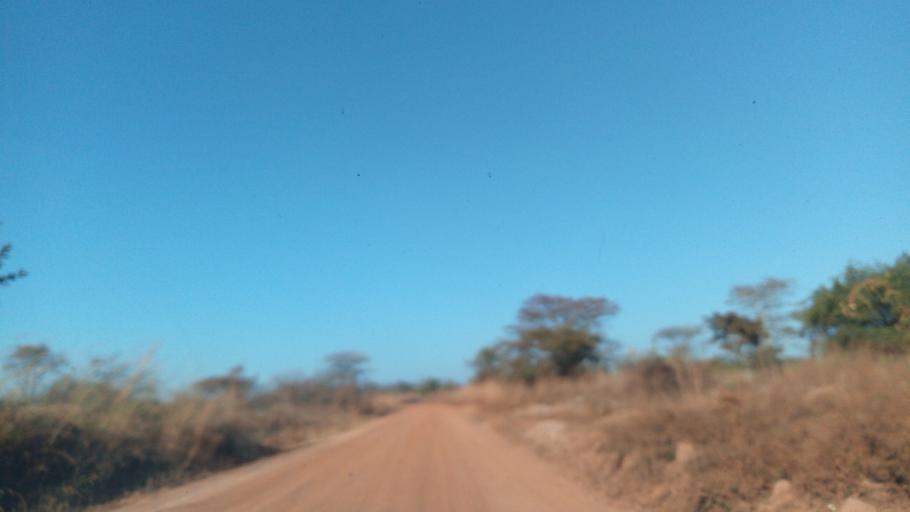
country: ZM
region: Luapula
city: Mwense
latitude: -10.5208
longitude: 28.4571
